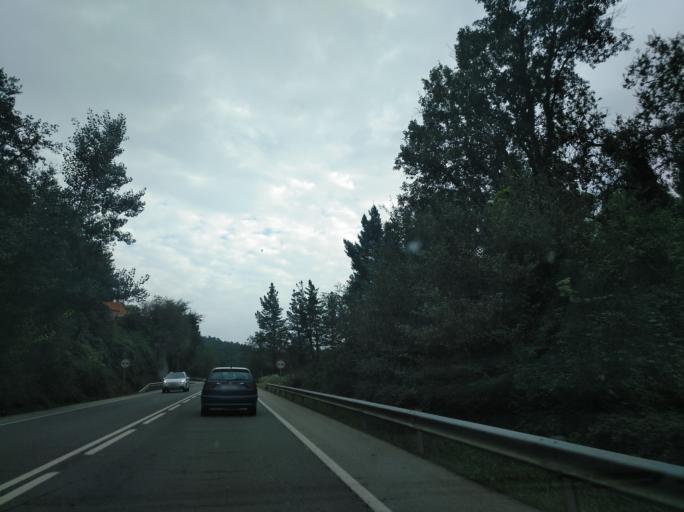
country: ES
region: Catalonia
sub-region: Provincia de Girona
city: Angles
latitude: 41.9481
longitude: 2.6412
